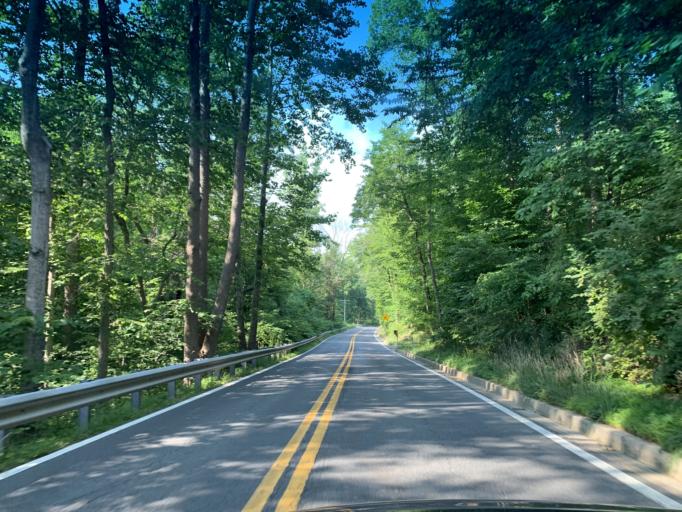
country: US
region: Maryland
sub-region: Frederick County
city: Urbana
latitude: 39.2718
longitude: -77.3391
